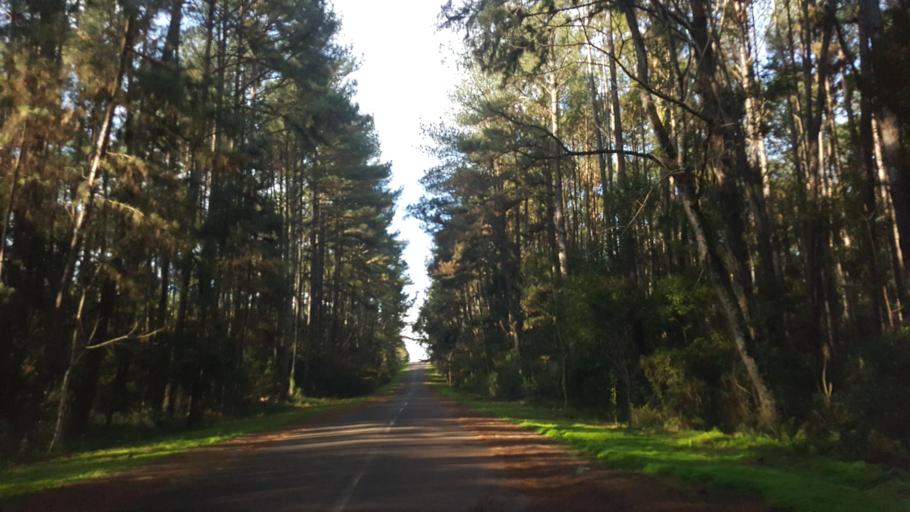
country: AR
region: Misiones
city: Puerto Leoni
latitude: -27.0045
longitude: -55.1877
